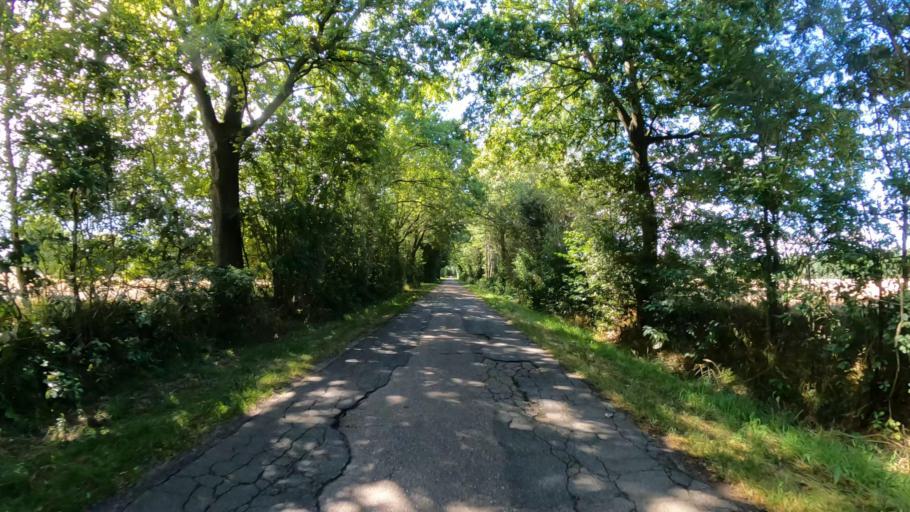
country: DE
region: Schleswig-Holstein
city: Hardebek
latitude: 53.9830
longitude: 9.8810
